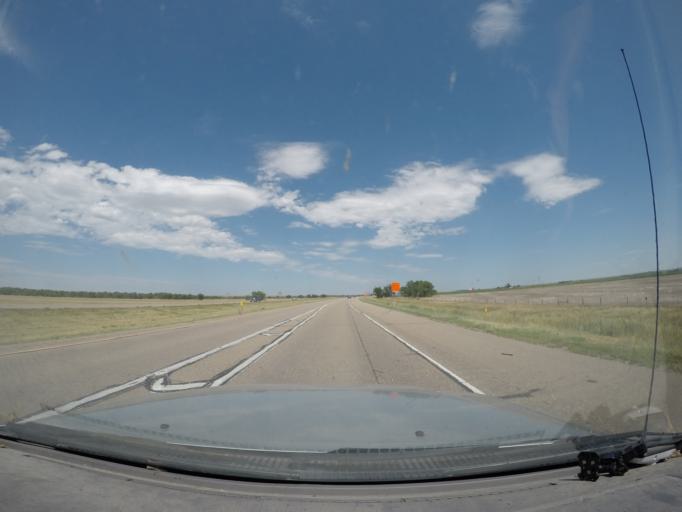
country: US
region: Colorado
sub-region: Sedgwick County
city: Julesburg
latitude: 41.0338
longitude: -102.1419
